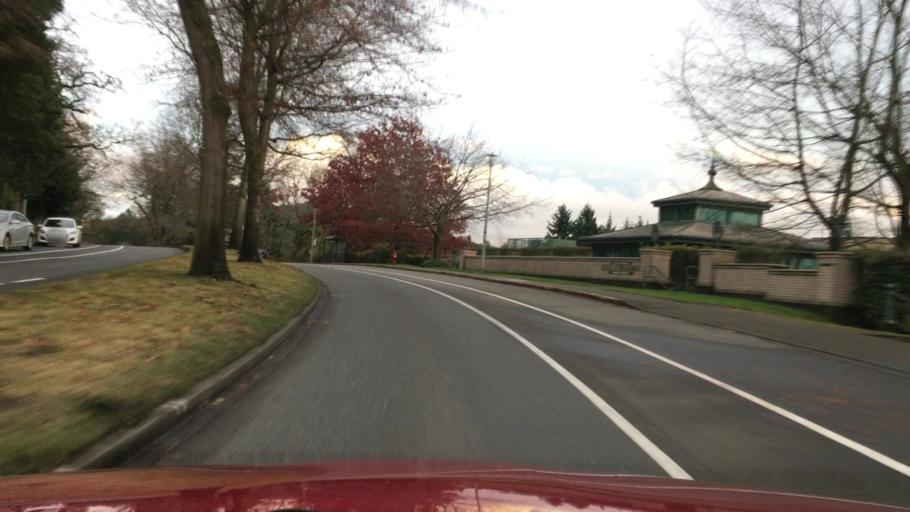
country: CA
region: British Columbia
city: Victoria
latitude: 48.4976
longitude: -123.3787
